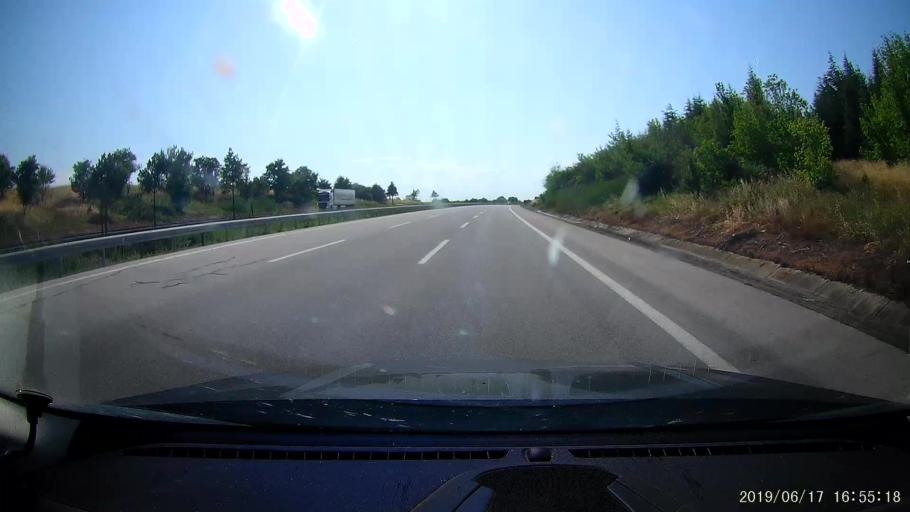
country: TR
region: Edirne
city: Haskoy
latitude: 41.5782
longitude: 26.9698
